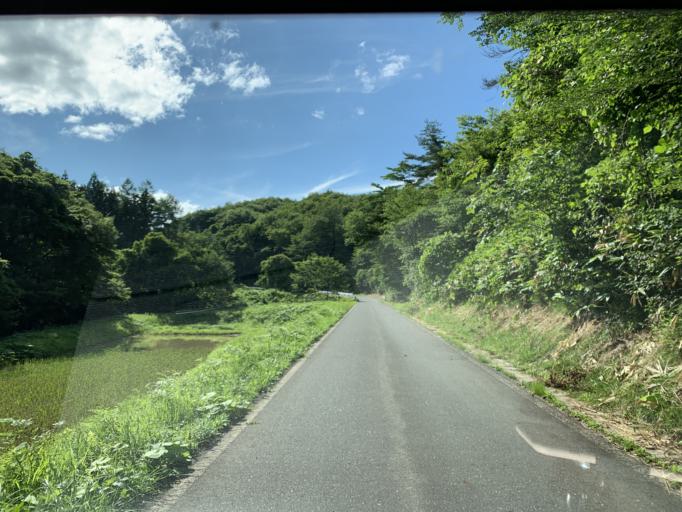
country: JP
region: Iwate
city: Ichinoseki
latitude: 38.9208
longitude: 140.9677
